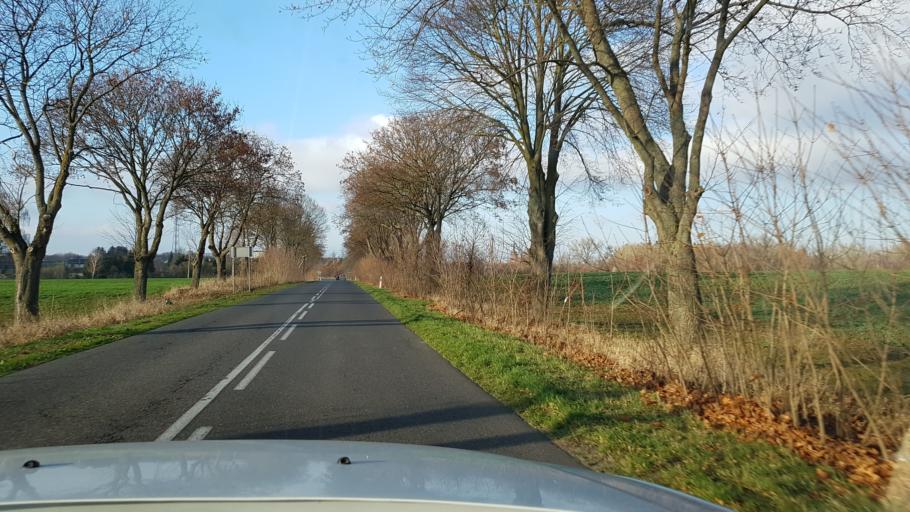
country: PL
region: West Pomeranian Voivodeship
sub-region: Powiat stargardzki
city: Chociwel
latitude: 53.4538
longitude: 15.3418
